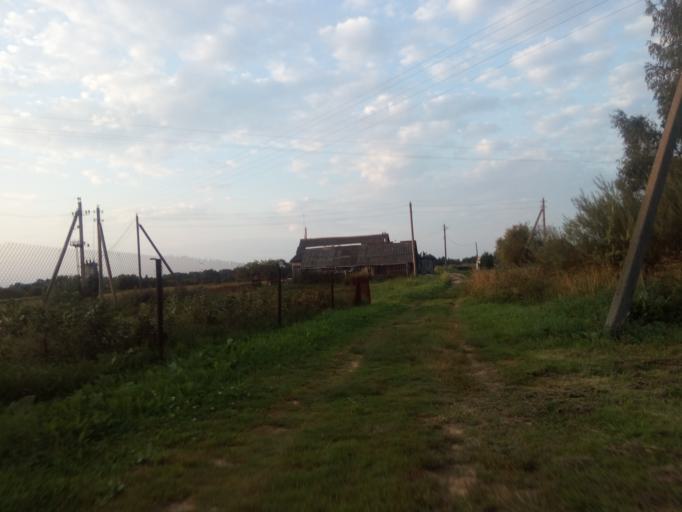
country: BY
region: Vitebsk
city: Dzisna
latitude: 55.6598
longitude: 28.3316
